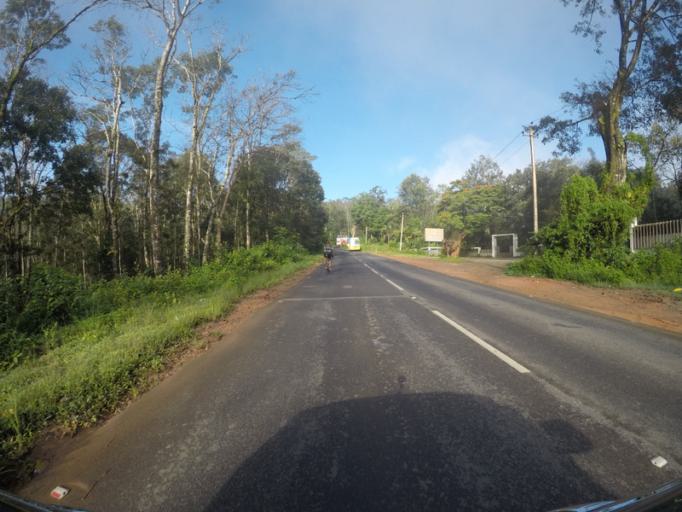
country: IN
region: Karnataka
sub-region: Kodagu
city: Madikeri
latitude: 12.4286
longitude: 75.7630
